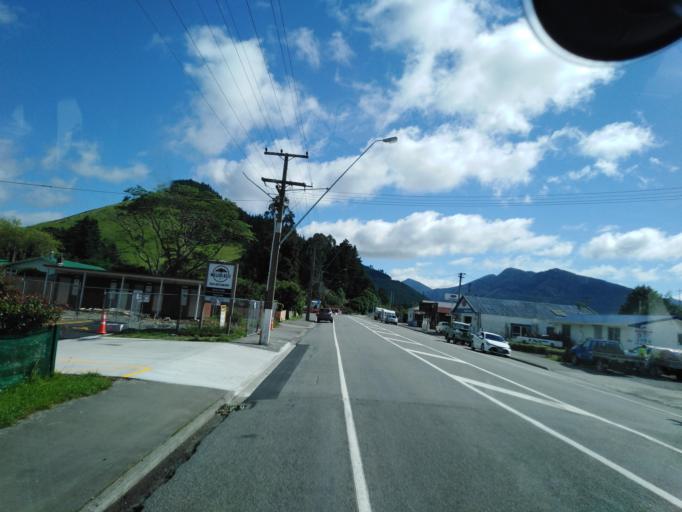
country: NZ
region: Nelson
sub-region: Nelson City
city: Nelson
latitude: -41.2288
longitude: 173.5827
